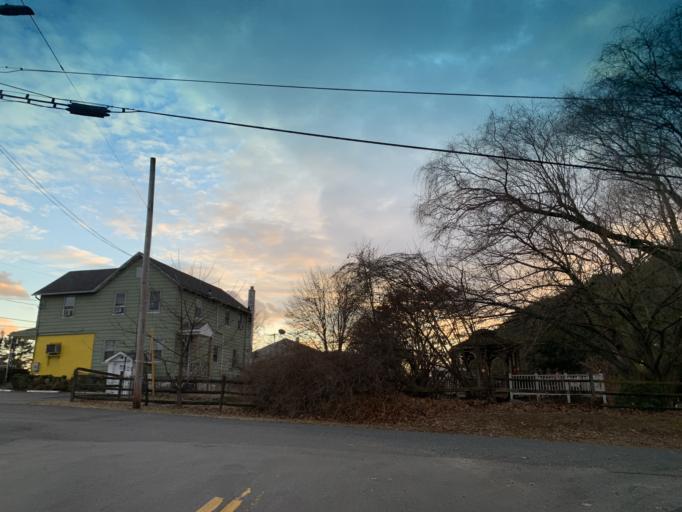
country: US
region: Maryland
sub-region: Harford County
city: South Bel Air
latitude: 39.5941
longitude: -76.3231
